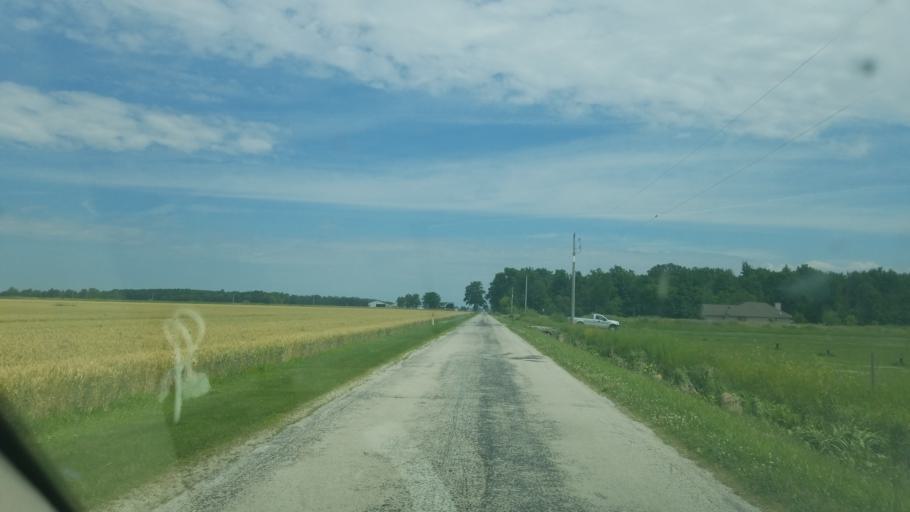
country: US
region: Ohio
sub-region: Wood County
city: North Baltimore
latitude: 41.2041
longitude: -83.5733
